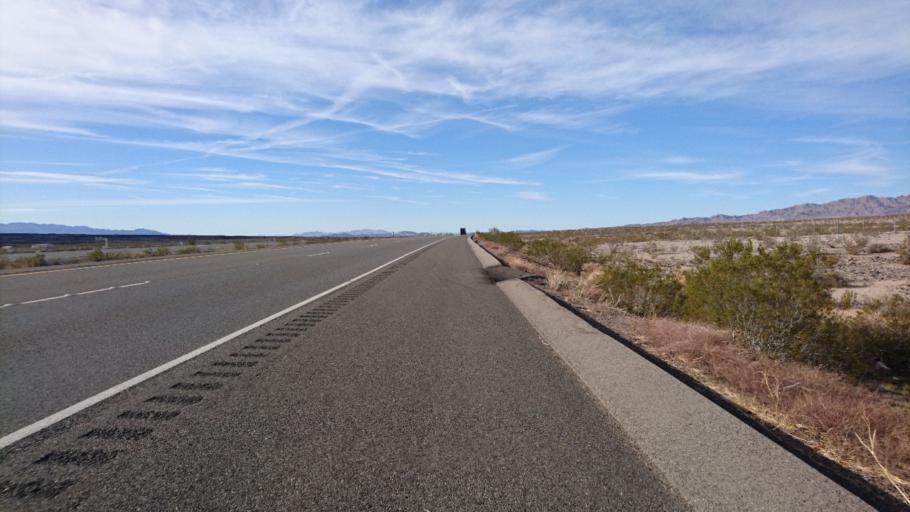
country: US
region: California
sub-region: San Bernardino County
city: Fort Irwin
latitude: 34.7527
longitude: -116.3385
